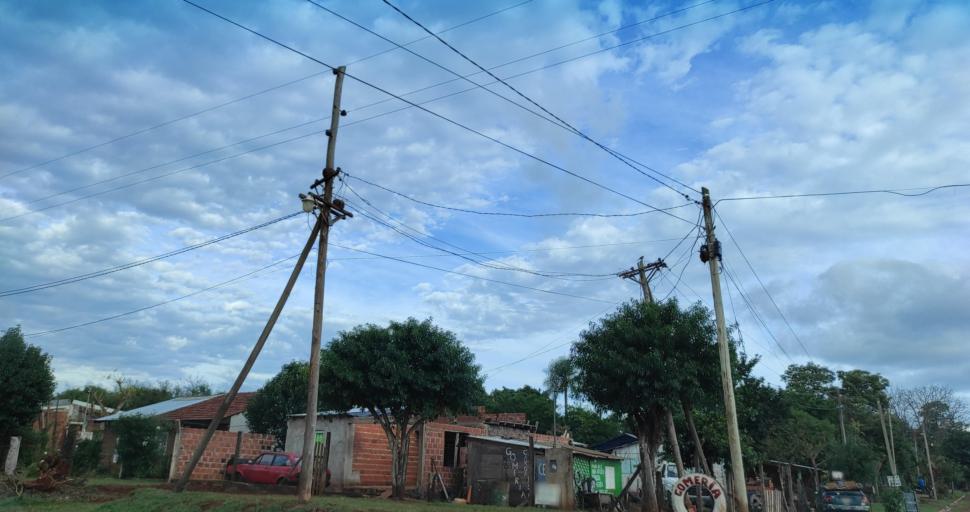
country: AR
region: Misiones
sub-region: Departamento de Candelaria
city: Candelaria
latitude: -27.4628
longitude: -55.7344
